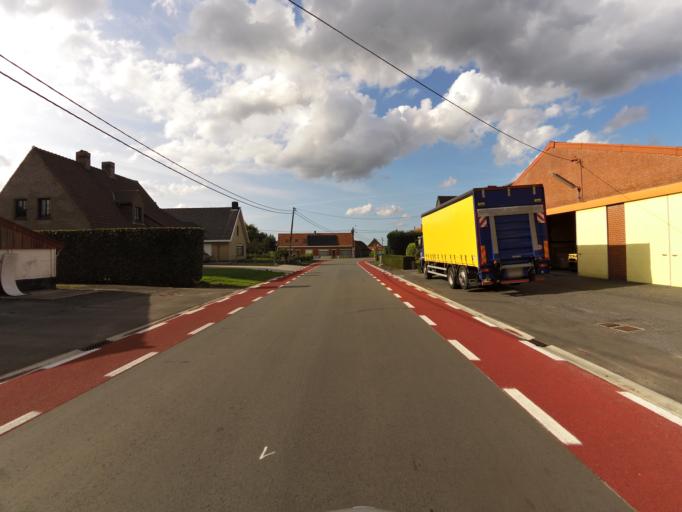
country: BE
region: Flanders
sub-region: Provincie West-Vlaanderen
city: Wingene
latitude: 51.0768
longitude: 3.2796
